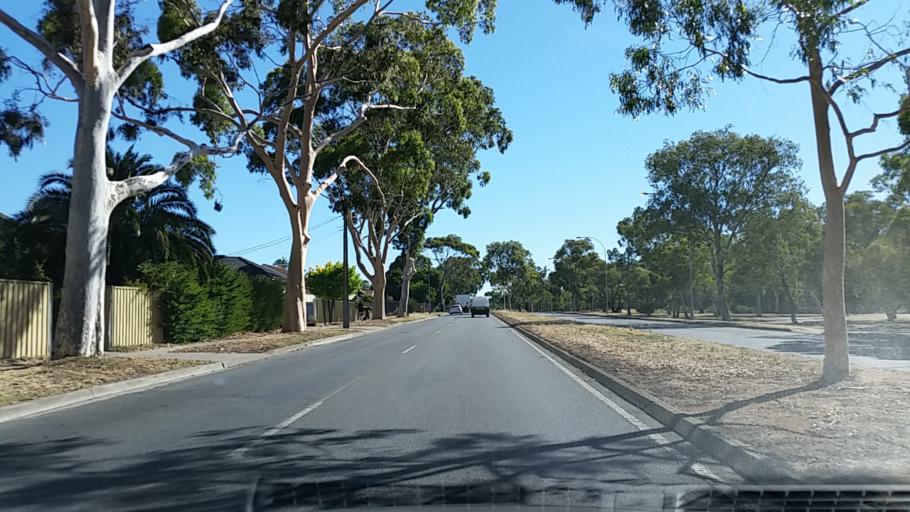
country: AU
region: South Australia
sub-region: Salisbury
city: Ingle Farm
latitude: -34.8122
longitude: 138.6444
